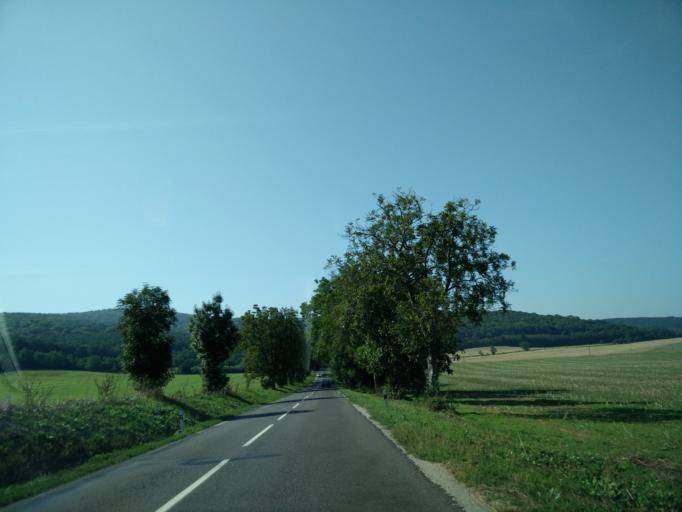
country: SK
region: Nitriansky
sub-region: Okres Nitra
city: Nitra
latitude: 48.3769
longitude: 18.0919
